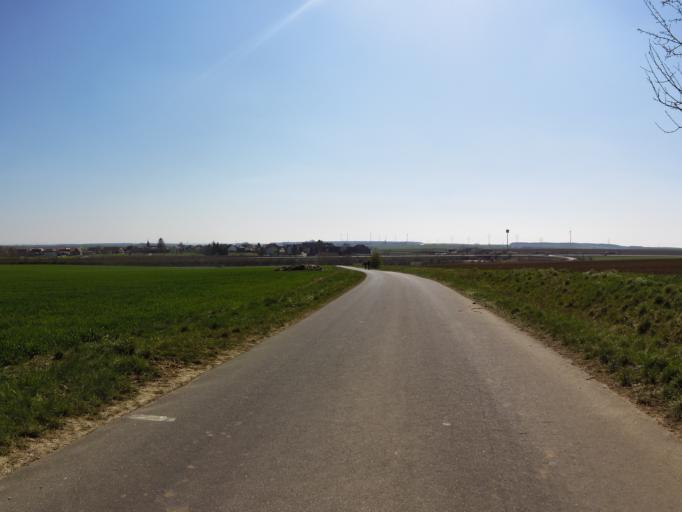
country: DE
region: Bavaria
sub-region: Regierungsbezirk Unterfranken
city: Biebelried
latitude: 49.7716
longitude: 10.0805
